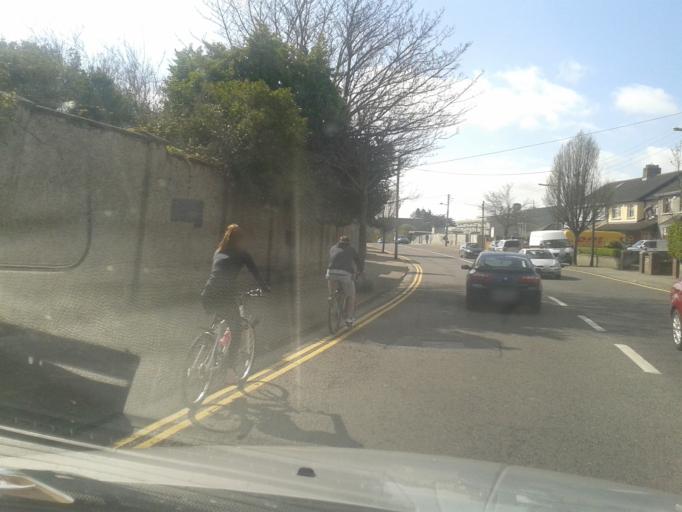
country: IE
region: Leinster
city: Raheny
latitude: 53.3825
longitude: -6.1762
